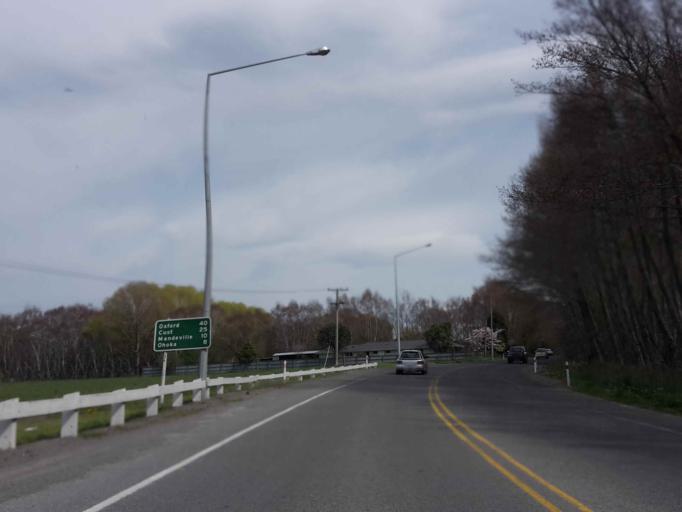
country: NZ
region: Canterbury
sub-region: Waimakariri District
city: Kaiapoi
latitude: -43.4085
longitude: 172.6409
